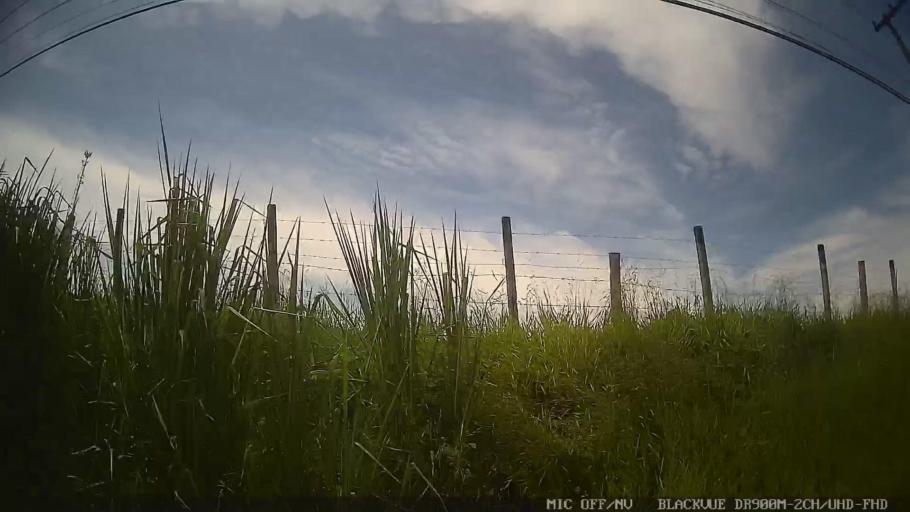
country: BR
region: Sao Paulo
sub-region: Santa Isabel
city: Santa Isabel
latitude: -23.3927
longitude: -46.1726
